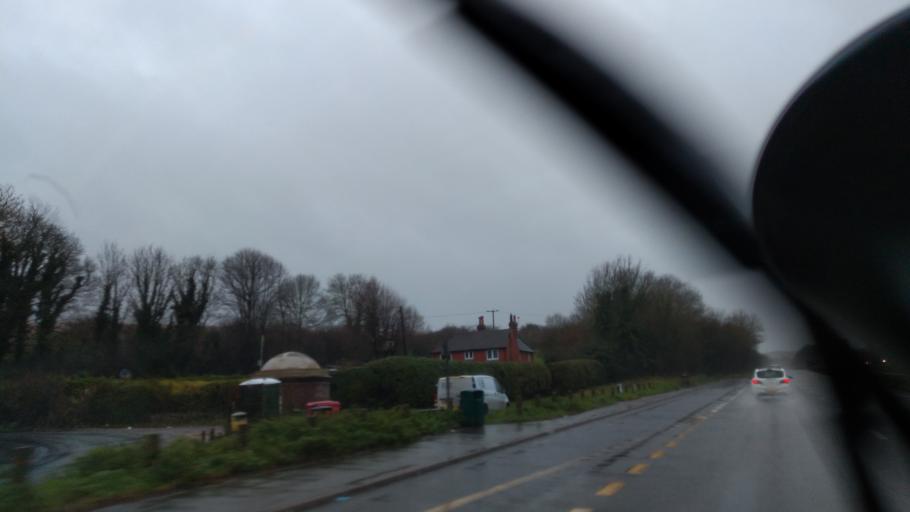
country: GB
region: England
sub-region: East Sussex
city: Lewes
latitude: 50.8665
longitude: -0.0263
